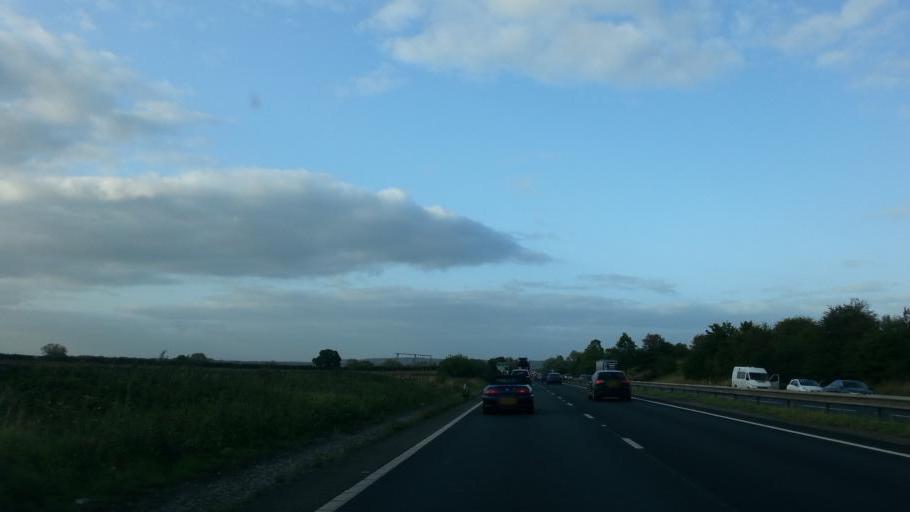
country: GB
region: England
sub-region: Oxfordshire
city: Marcham
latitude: 51.6554
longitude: -1.3172
